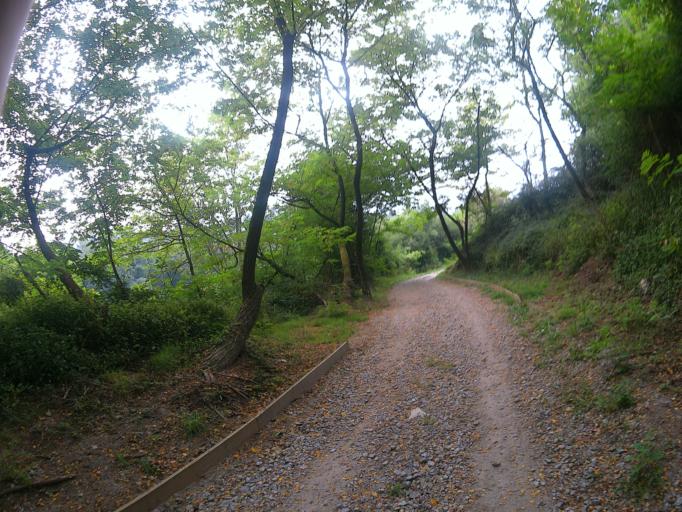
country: PT
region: Viana do Castelo
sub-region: Ponte de Lima
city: Ponte de Lima
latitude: 41.7907
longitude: -8.5147
